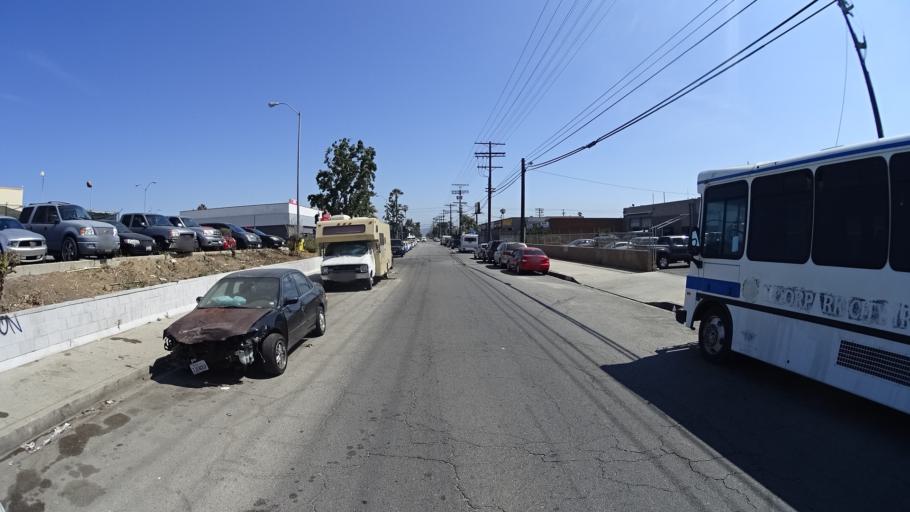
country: US
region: California
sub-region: Los Angeles County
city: Van Nuys
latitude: 34.2026
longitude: -118.4183
